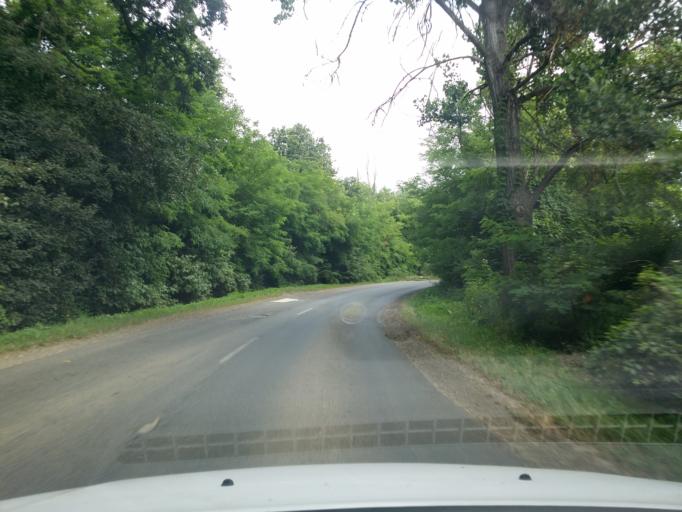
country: HU
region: Pest
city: Acsa
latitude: 47.8114
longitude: 19.3876
